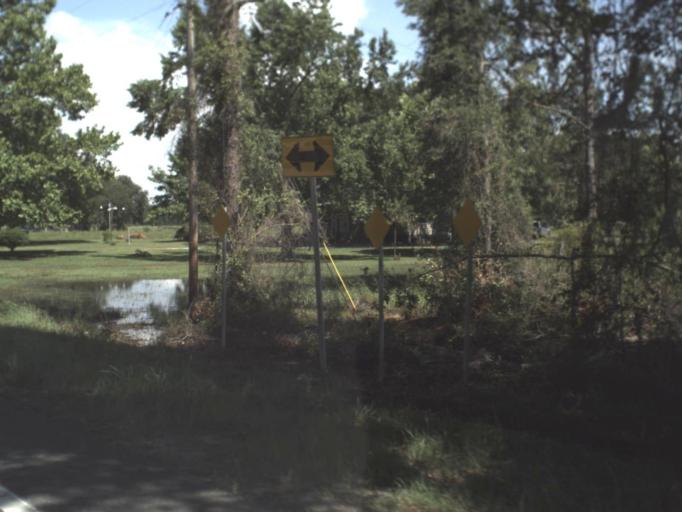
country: US
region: Florida
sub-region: Lafayette County
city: Mayo
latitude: 30.1292
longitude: -83.3397
